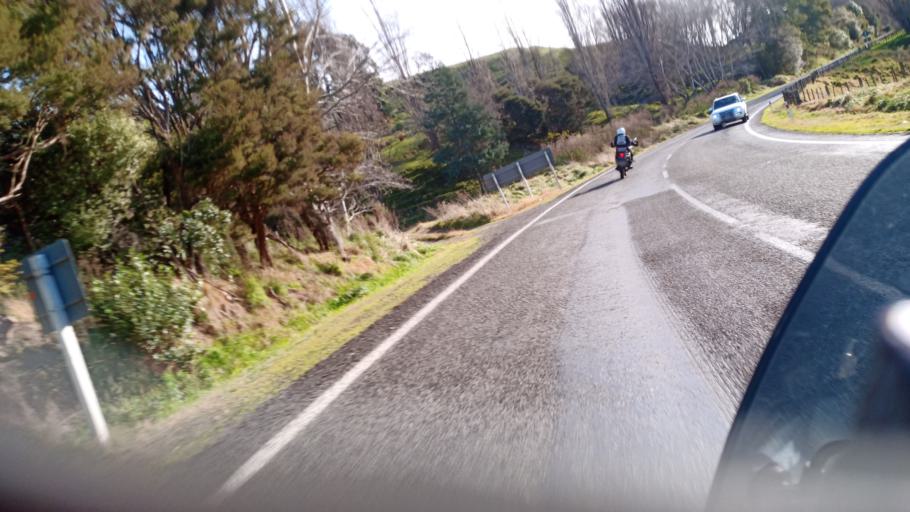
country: NZ
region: Gisborne
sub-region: Gisborne District
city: Gisborne
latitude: -38.4538
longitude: 177.6320
